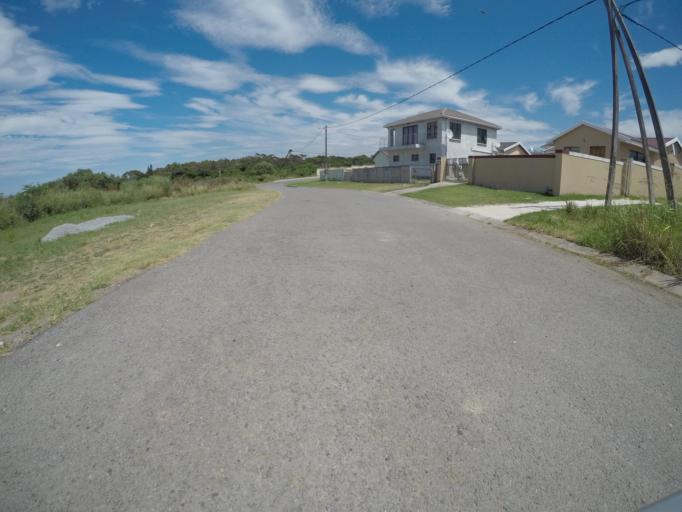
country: ZA
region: Eastern Cape
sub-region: Buffalo City Metropolitan Municipality
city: East London
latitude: -33.0439
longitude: 27.8659
